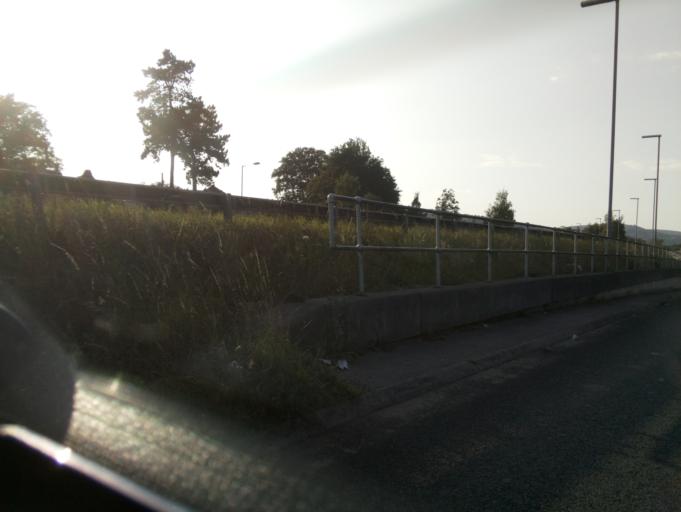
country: GB
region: Wales
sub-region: Torfaen County Borough
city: Pontypool
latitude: 51.6970
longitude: -3.0280
